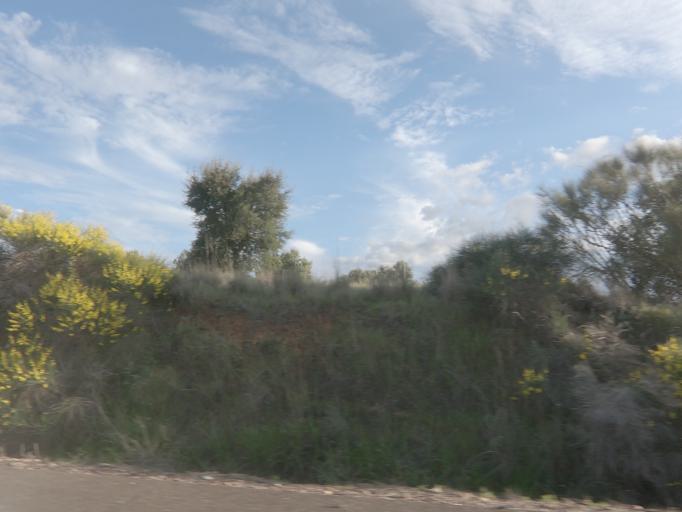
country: ES
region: Extremadura
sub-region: Provincia de Badajoz
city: Talavera La Real
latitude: 38.8660
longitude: -6.7964
